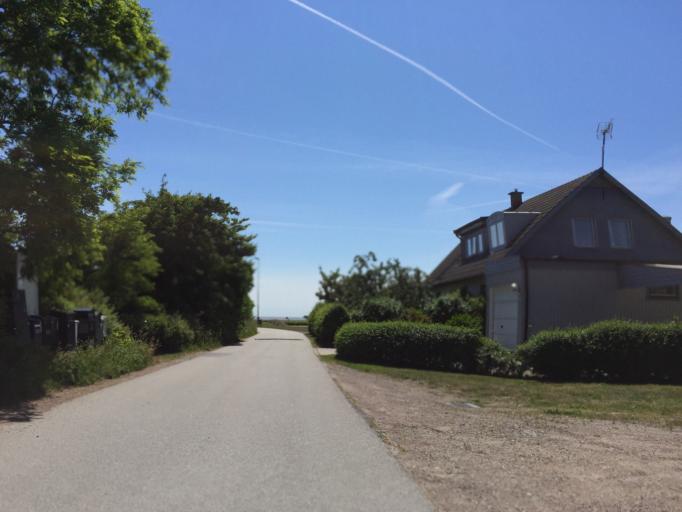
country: SE
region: Skane
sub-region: Trelleborgs Kommun
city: Skare
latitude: 55.3736
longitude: 13.0827
